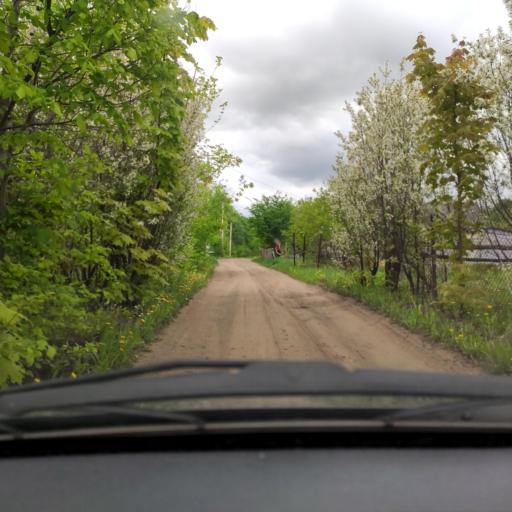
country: RU
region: Bashkortostan
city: Kabakovo
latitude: 54.7068
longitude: 56.1603
